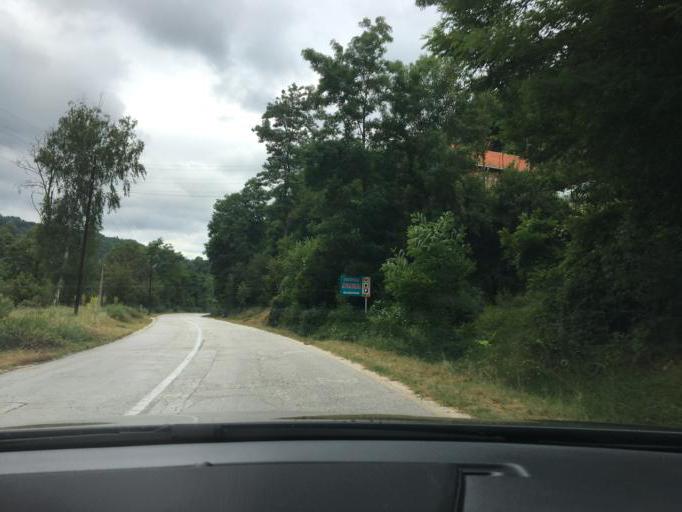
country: MK
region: Kriva Palanka
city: Kriva Palanka
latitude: 42.2253
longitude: 22.4064
